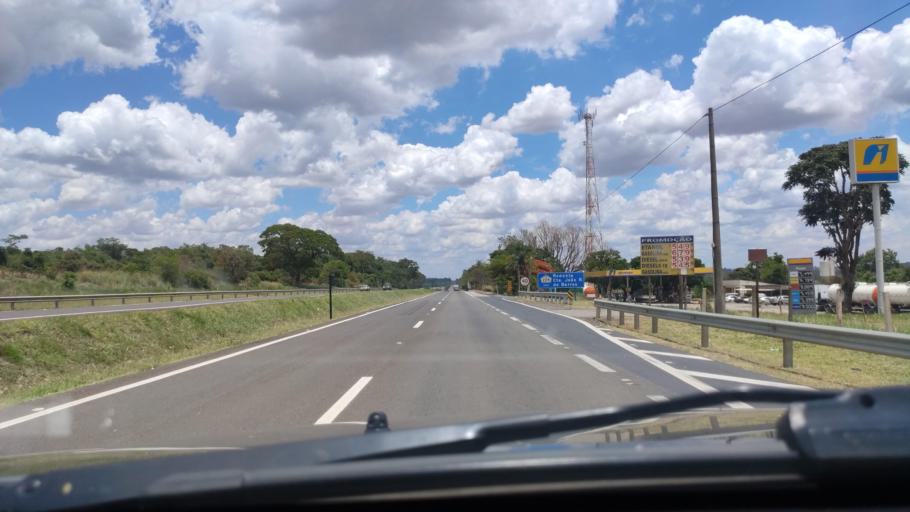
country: BR
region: Sao Paulo
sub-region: Pederneiras
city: Pederneiras
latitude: -22.3315
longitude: -48.9140
